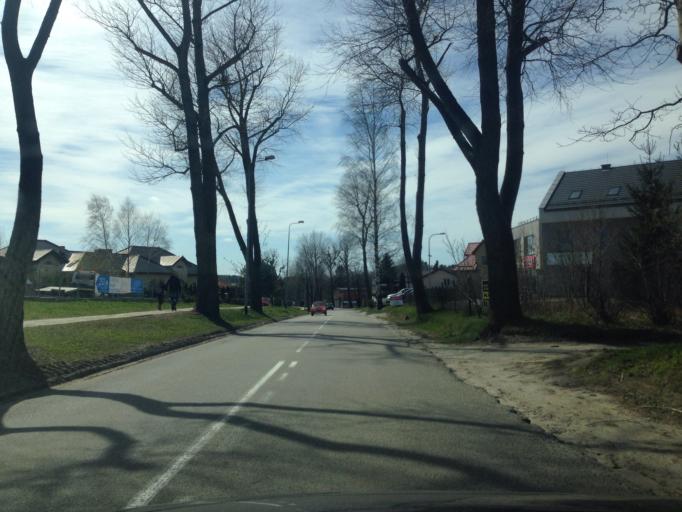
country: PL
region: Pomeranian Voivodeship
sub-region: Powiat wejherowski
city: Bojano
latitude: 54.4934
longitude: 18.4291
